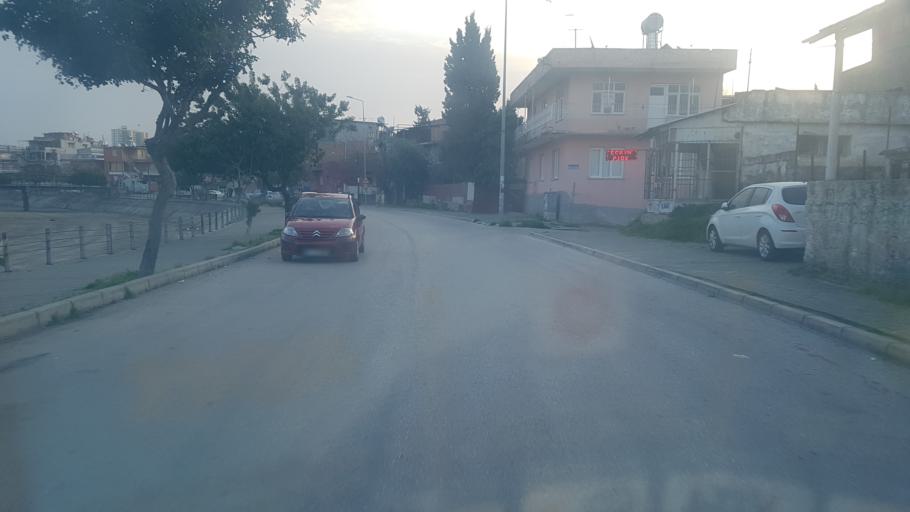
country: TR
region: Adana
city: Adana
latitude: 37.0091
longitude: 35.3271
